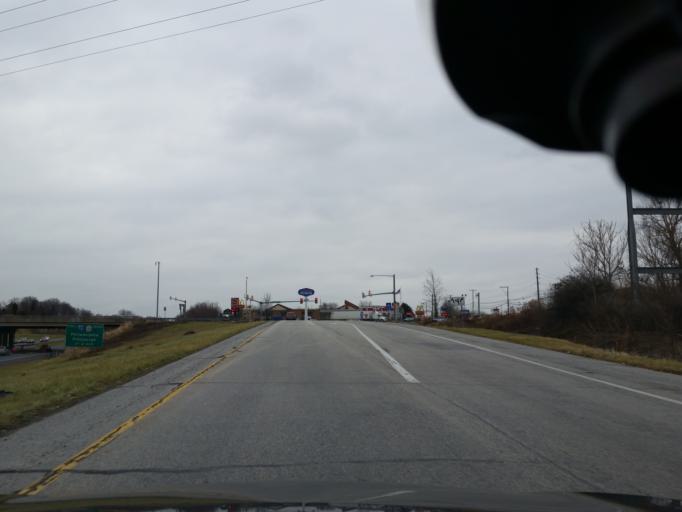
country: US
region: Pennsylvania
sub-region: Dauphin County
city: Lawnton
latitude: 40.2434
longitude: -76.8071
